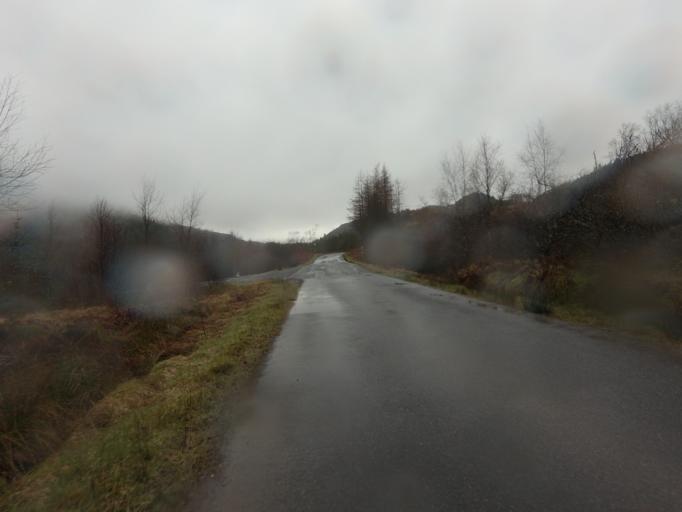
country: GB
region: Scotland
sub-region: West Dunbartonshire
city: Balloch
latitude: 56.2341
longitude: -4.5604
